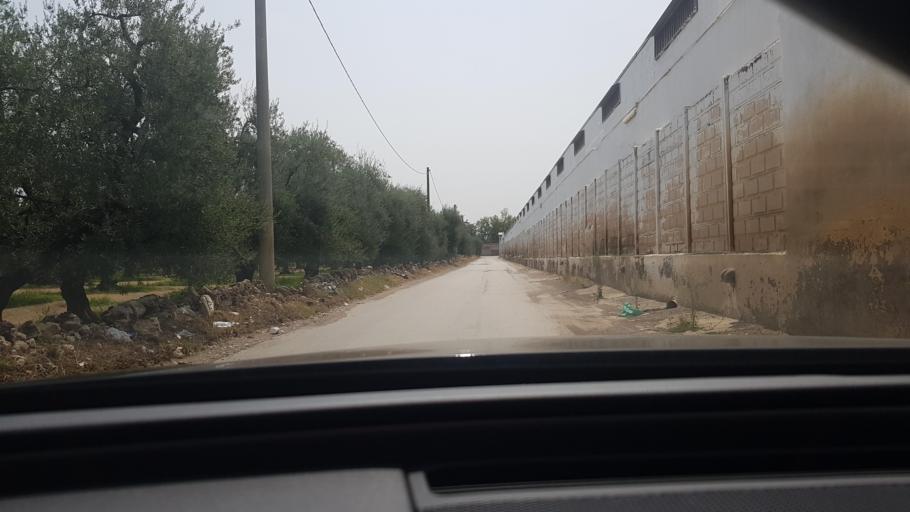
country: IT
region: Apulia
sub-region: Provincia di Barletta - Andria - Trani
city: Andria
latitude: 41.2171
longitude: 16.2603
